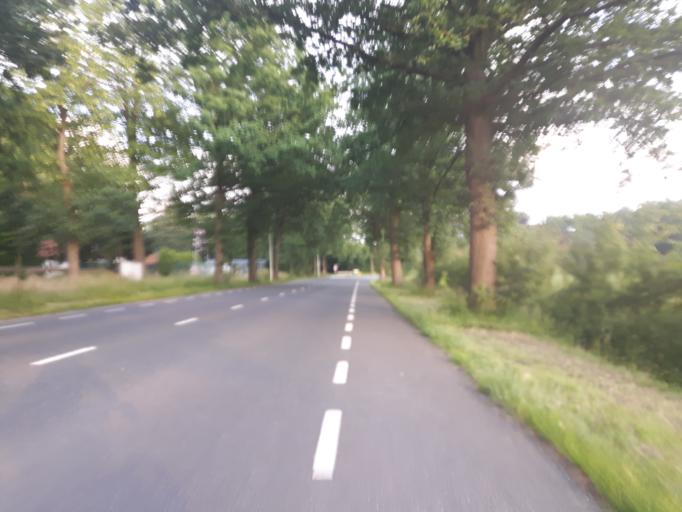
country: NL
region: Overijssel
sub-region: Gemeente Hengelo
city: Hengelo
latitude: 52.2433
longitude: 6.8090
